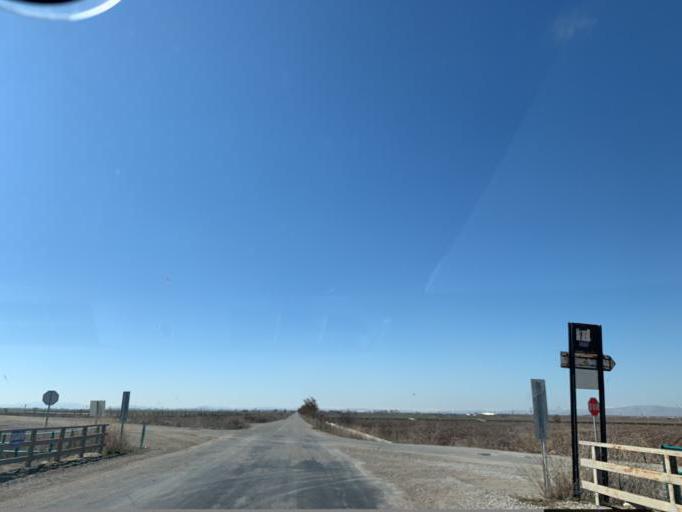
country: TR
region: Konya
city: Catalhoeyuek
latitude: 37.6290
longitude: 32.8083
